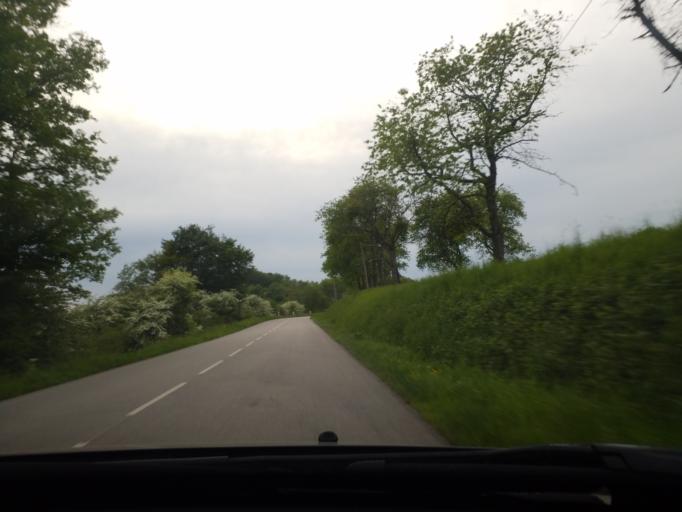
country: FR
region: Lorraine
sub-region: Departement des Vosges
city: Bains-les-Bains
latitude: 48.0321
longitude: 6.1911
